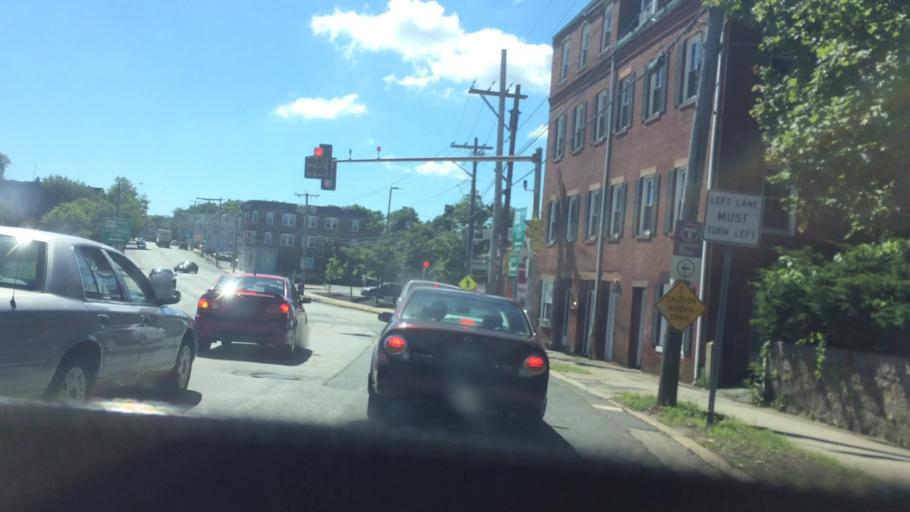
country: US
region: Massachusetts
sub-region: Essex County
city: Salem
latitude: 42.5192
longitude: -70.9099
